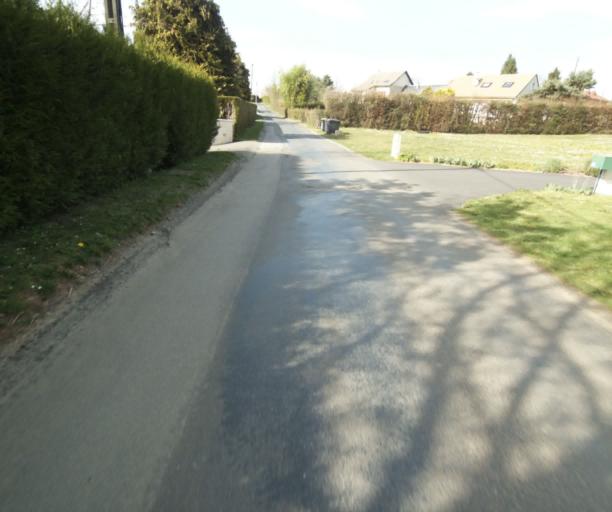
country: FR
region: Limousin
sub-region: Departement de la Correze
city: Naves
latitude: 45.3346
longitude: 1.7499
